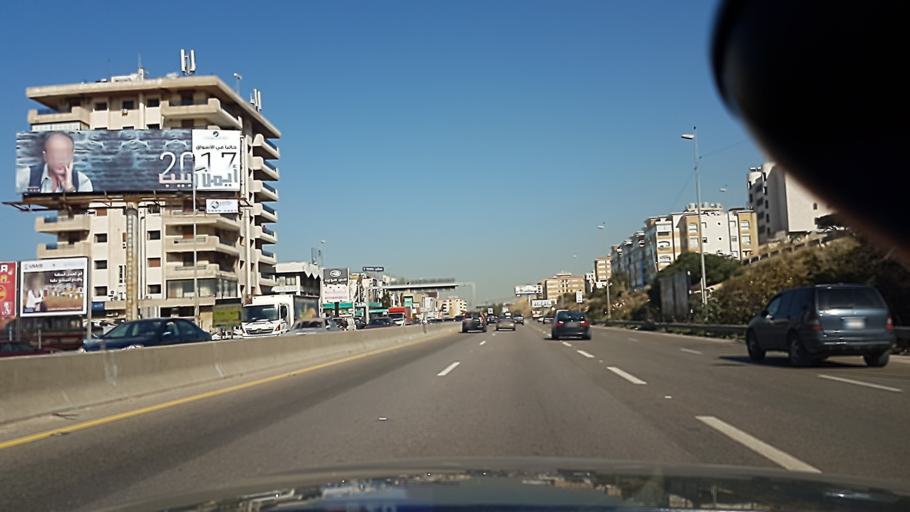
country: LB
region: Mont-Liban
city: Baabda
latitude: 33.7900
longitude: 35.4809
